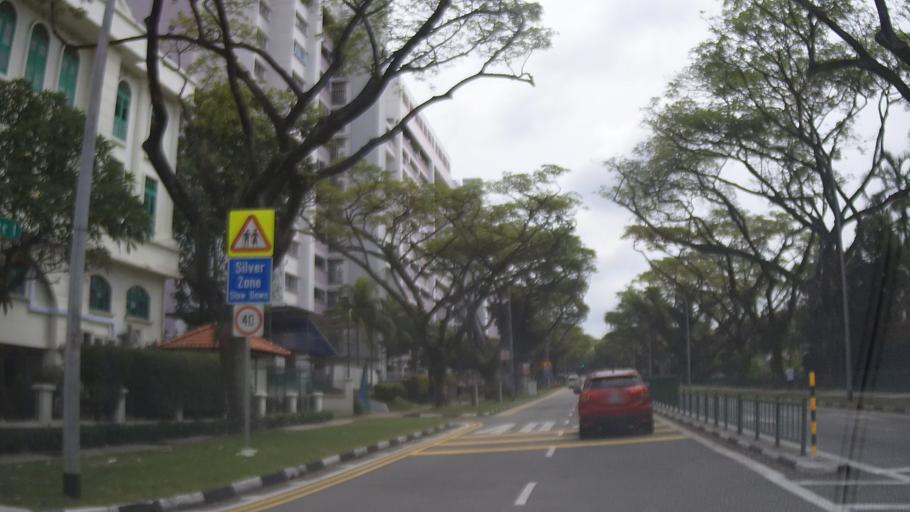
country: MY
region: Johor
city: Johor Bahru
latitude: 1.4292
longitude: 103.7754
